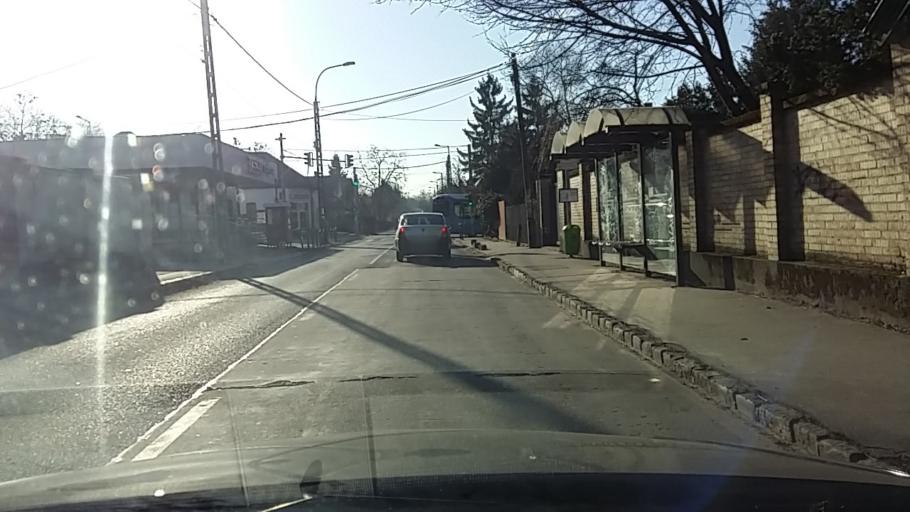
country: HU
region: Budapest
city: Budapest XVI. keruelet
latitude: 47.5238
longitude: 19.1716
